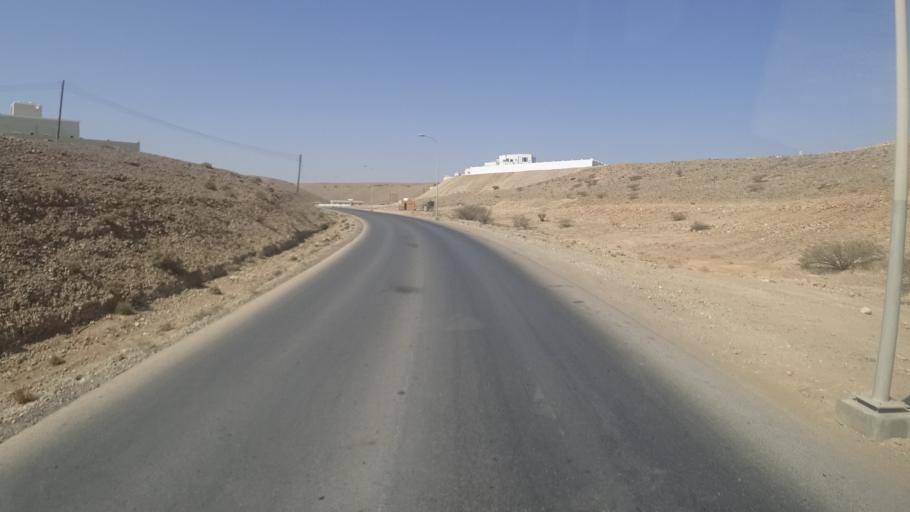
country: OM
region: Ash Sharqiyah
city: Sur
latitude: 22.5452
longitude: 59.4988
